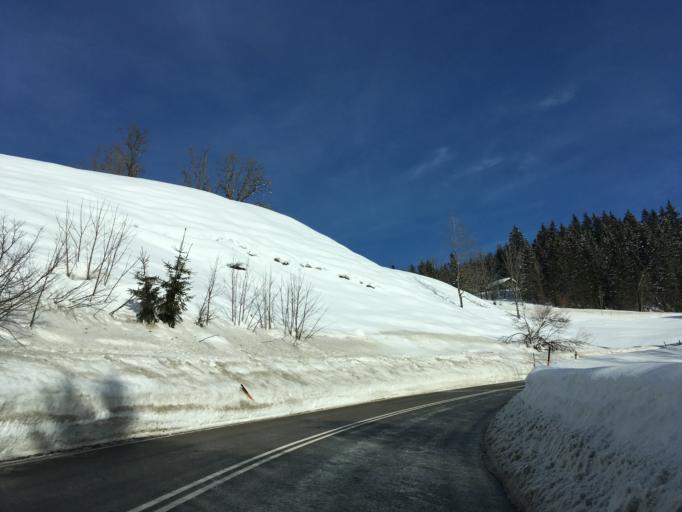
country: DE
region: Bavaria
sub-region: Upper Bavaria
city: Burg Unter-Falkenstein
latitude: 47.6720
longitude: 12.0693
